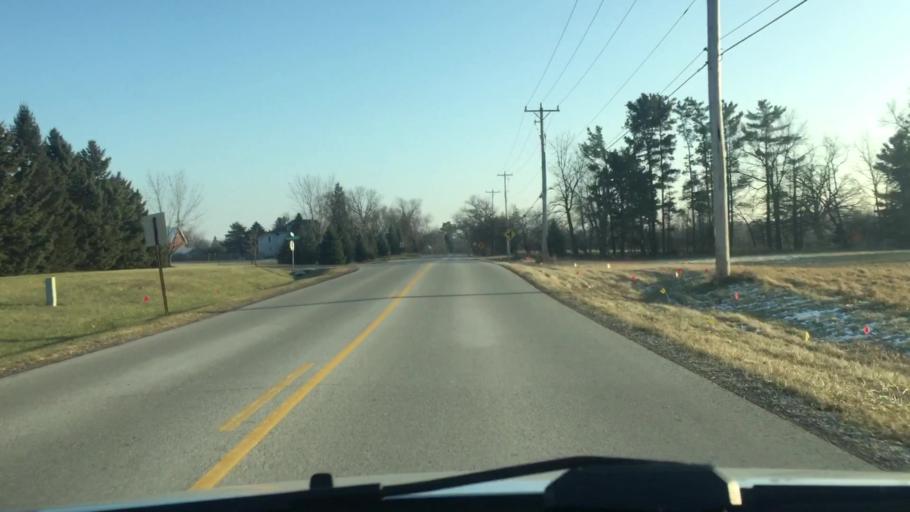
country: US
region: Wisconsin
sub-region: Waukesha County
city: Dousman
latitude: 43.0355
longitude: -88.4821
